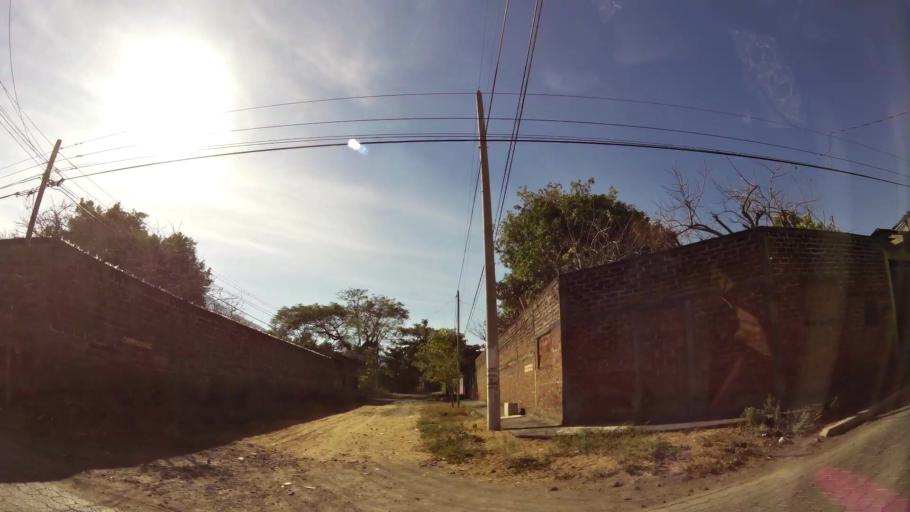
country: SV
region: San Miguel
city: San Miguel
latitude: 13.4739
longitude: -88.1938
